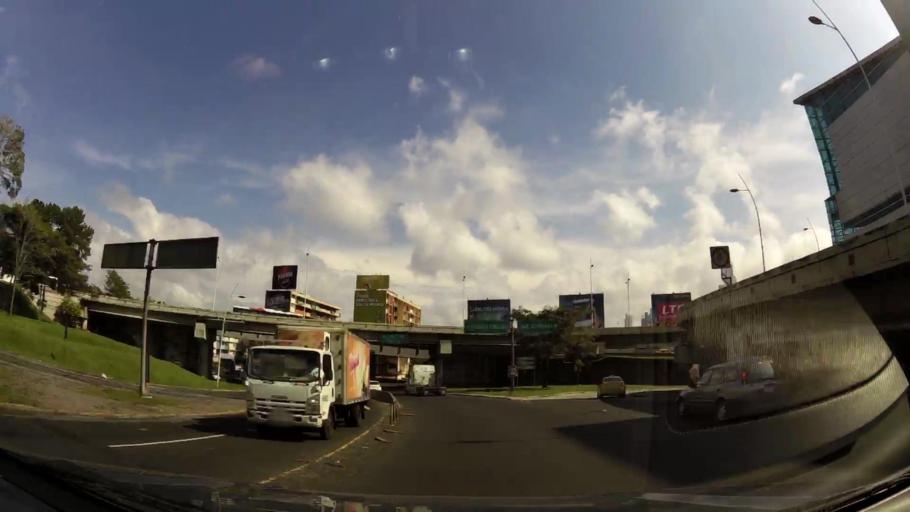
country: PA
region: Panama
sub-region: Distrito de Panama
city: Ancon
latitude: 8.9633
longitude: -79.5425
